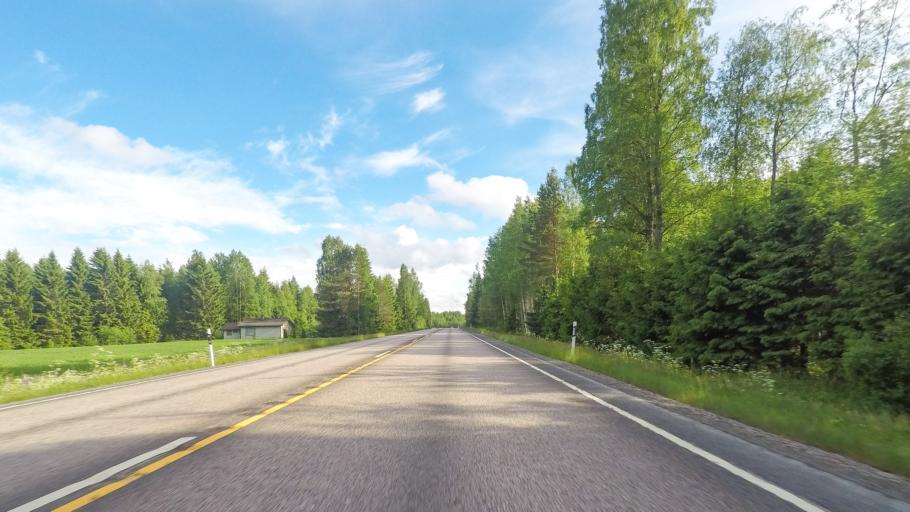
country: FI
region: Central Finland
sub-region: Joutsa
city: Leivonmaeki
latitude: 61.8866
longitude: 26.1130
